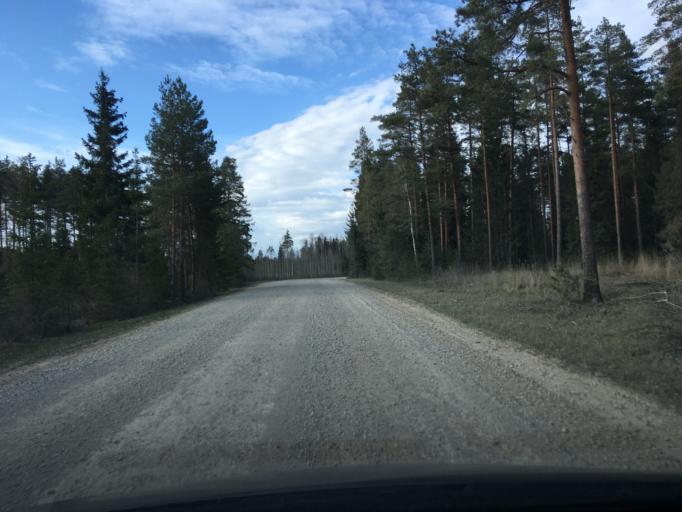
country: EE
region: Raplamaa
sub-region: Maerjamaa vald
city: Marjamaa
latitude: 58.9566
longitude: 24.3259
